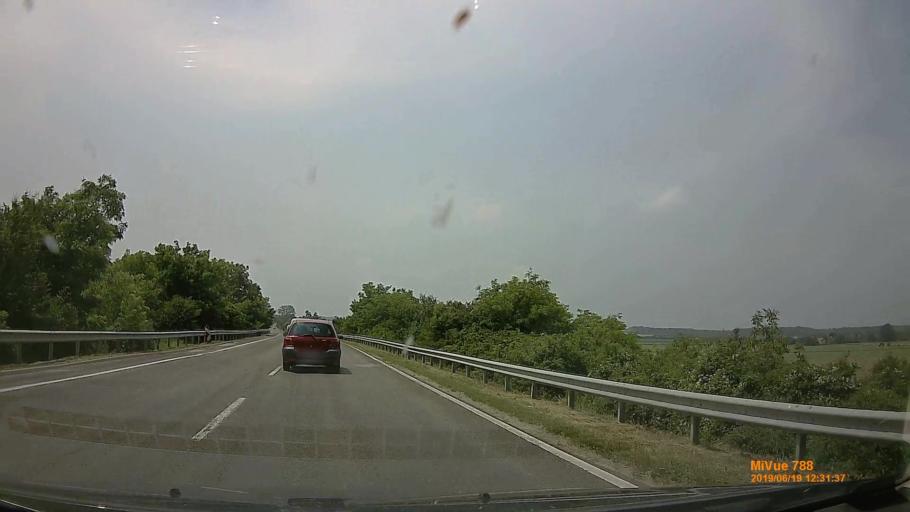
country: HU
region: Baranya
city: Szentlorinc
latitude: 46.0440
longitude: 17.9775
